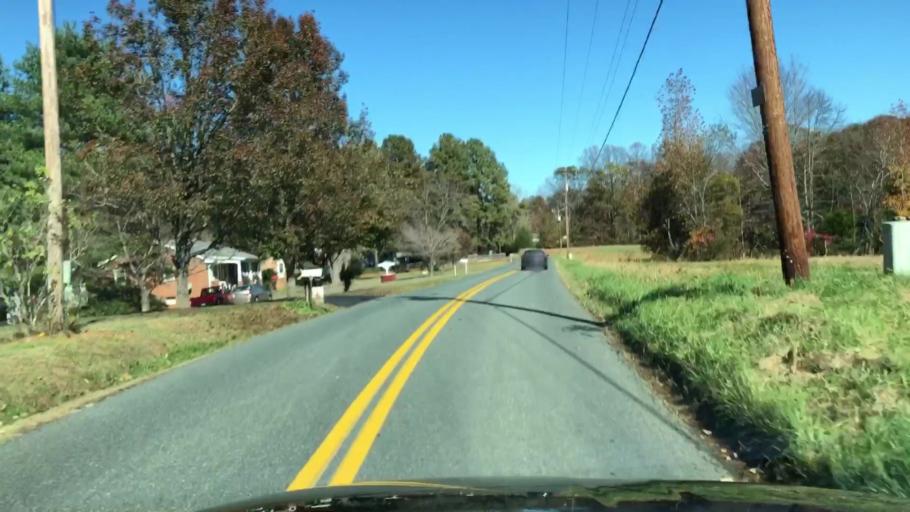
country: US
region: Virginia
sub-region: Stafford County
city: Falmouth
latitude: 38.3921
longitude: -77.5839
